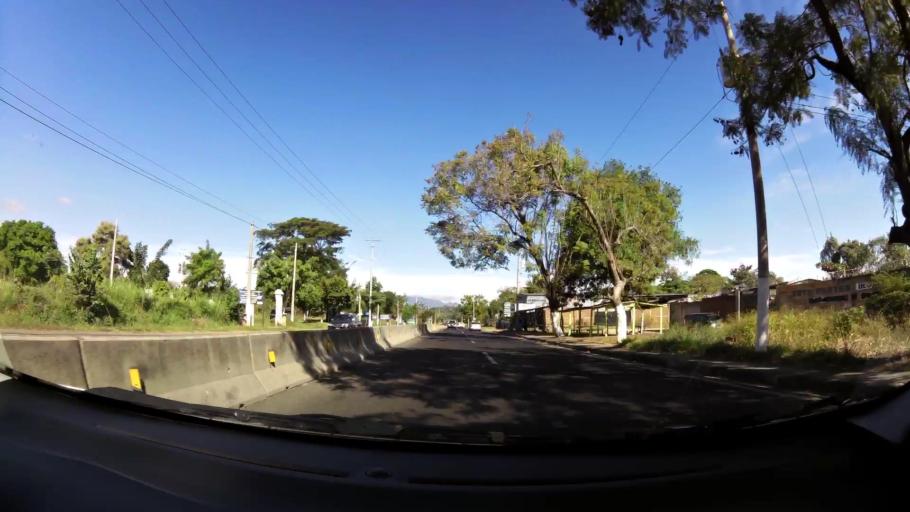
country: SV
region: Santa Ana
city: Santa Ana
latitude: 13.9645
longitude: -89.5803
